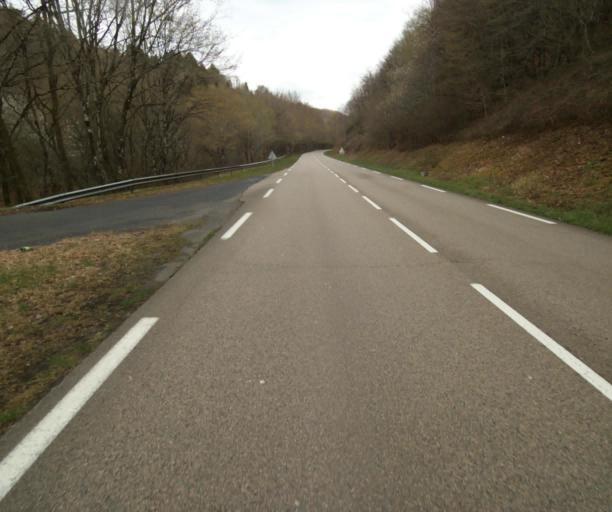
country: FR
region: Limousin
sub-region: Departement de la Correze
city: Sainte-Fortunade
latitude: 45.1861
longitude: 1.8462
